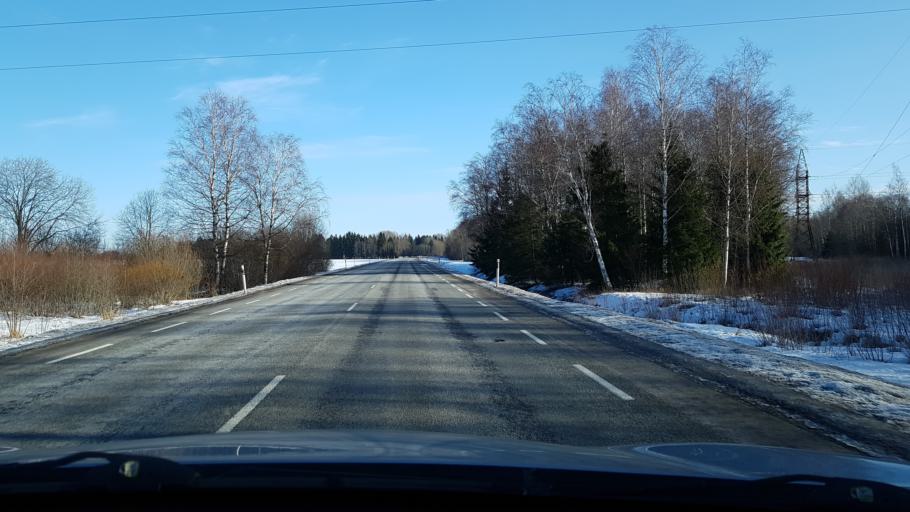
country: EE
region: Viljandimaa
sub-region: Vohma linn
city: Vohma
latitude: 58.6639
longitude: 25.6250
